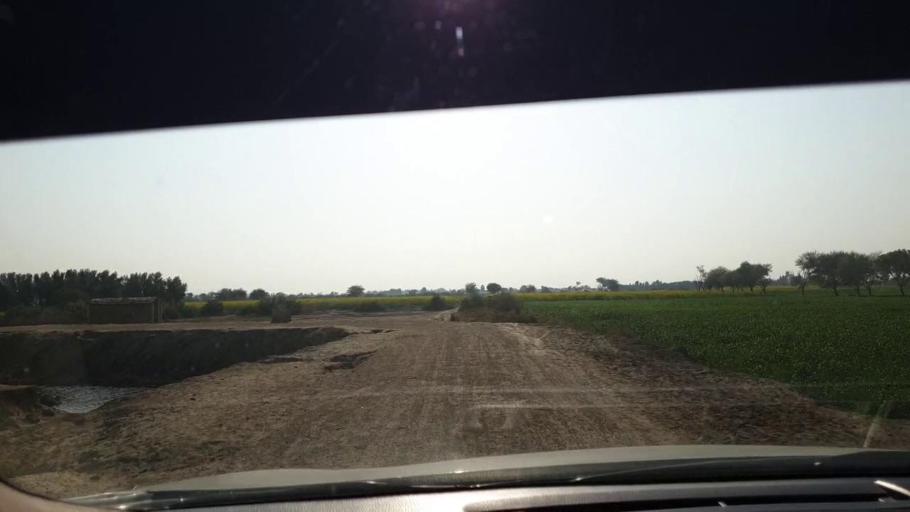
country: PK
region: Sindh
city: Berani
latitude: 25.8107
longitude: 68.7802
